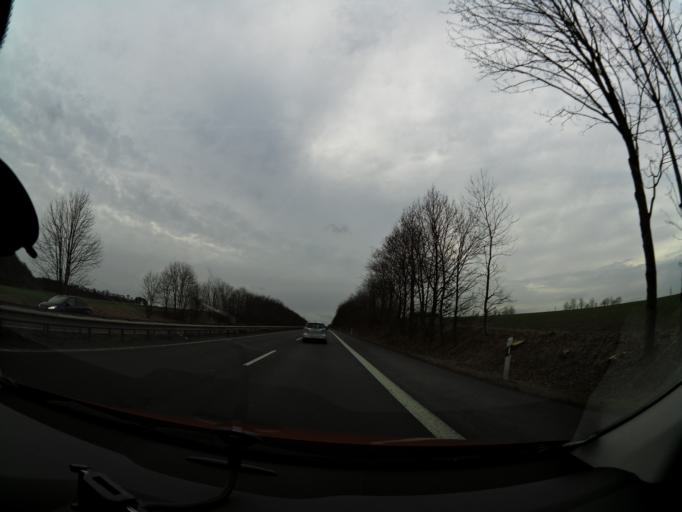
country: DE
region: Lower Saxony
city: Leiferde
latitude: 52.1983
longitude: 10.5260
